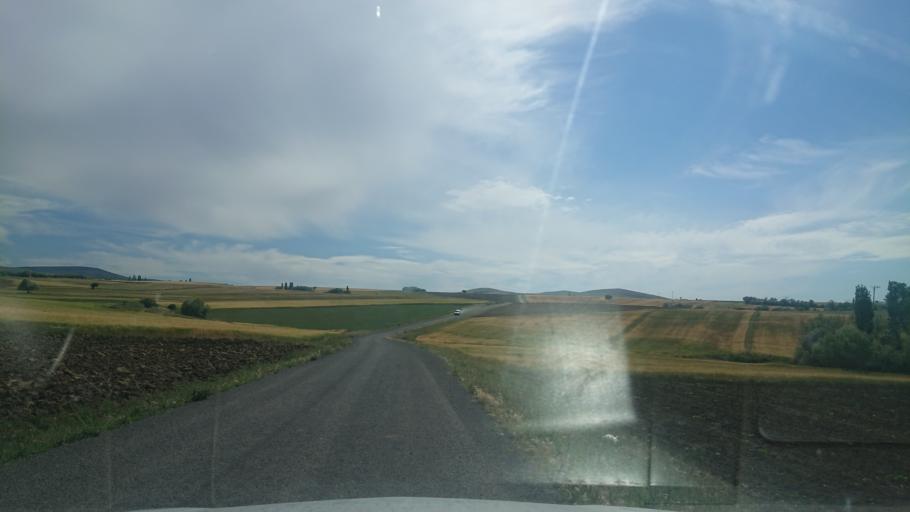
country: TR
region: Aksaray
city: Ortakoy
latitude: 38.8192
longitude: 34.0093
